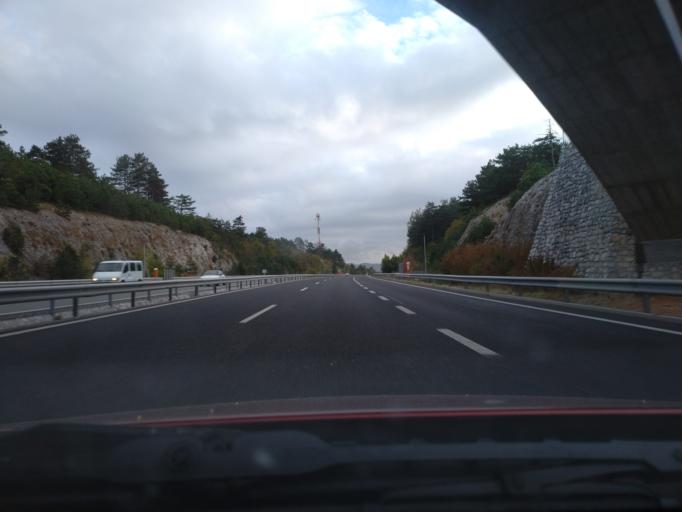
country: SI
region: Hrpelje-Kozina
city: Kozina
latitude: 45.6381
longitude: 13.9617
